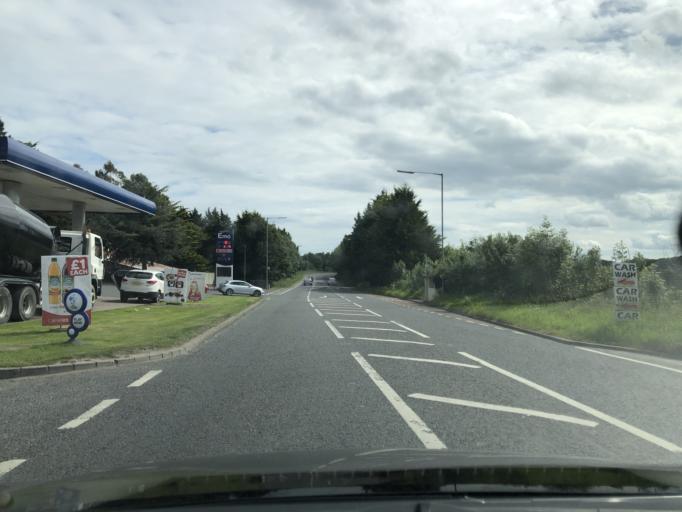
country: GB
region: Northern Ireland
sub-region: Down District
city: Dundrum
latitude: 54.3336
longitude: -5.8357
